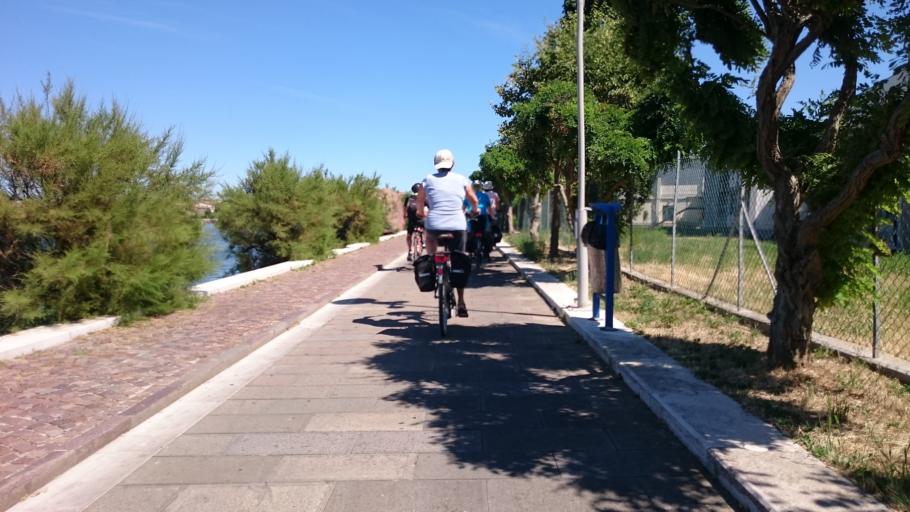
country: IT
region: Veneto
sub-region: Provincia di Venezia
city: Chioggia
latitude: 45.2033
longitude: 12.2794
